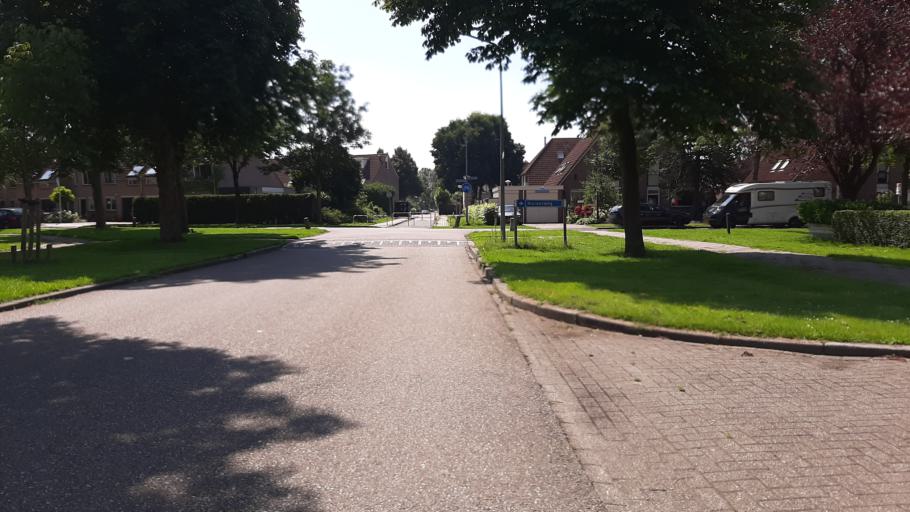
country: NL
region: Flevoland
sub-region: Gemeente Zeewolde
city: Zeewolde
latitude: 52.3357
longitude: 5.5302
